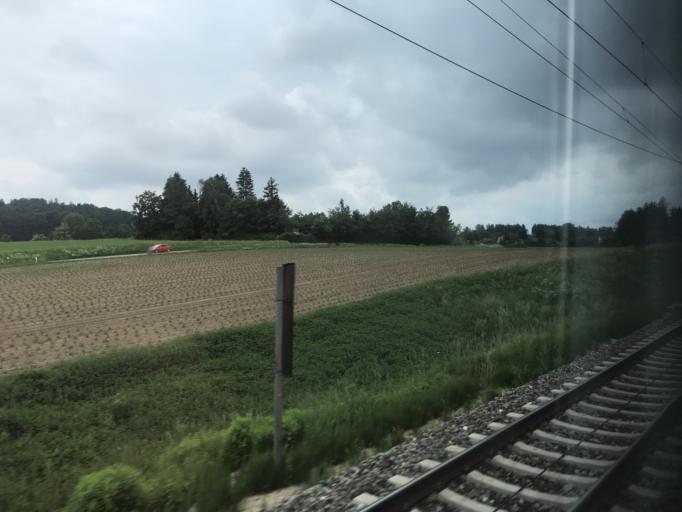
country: DE
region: Bavaria
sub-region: Swabia
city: Diedorf
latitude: 48.3742
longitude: 10.8021
